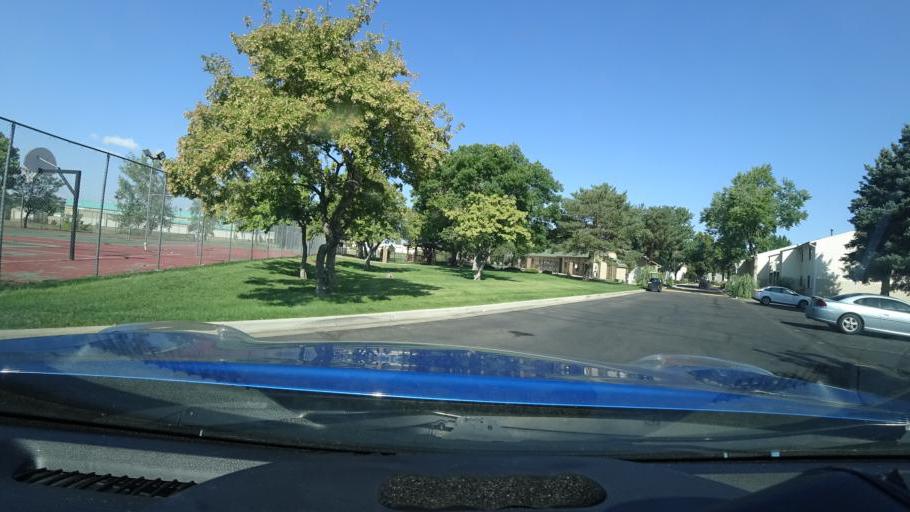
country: US
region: Colorado
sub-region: Adams County
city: Aurora
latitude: 39.7231
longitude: -104.8142
